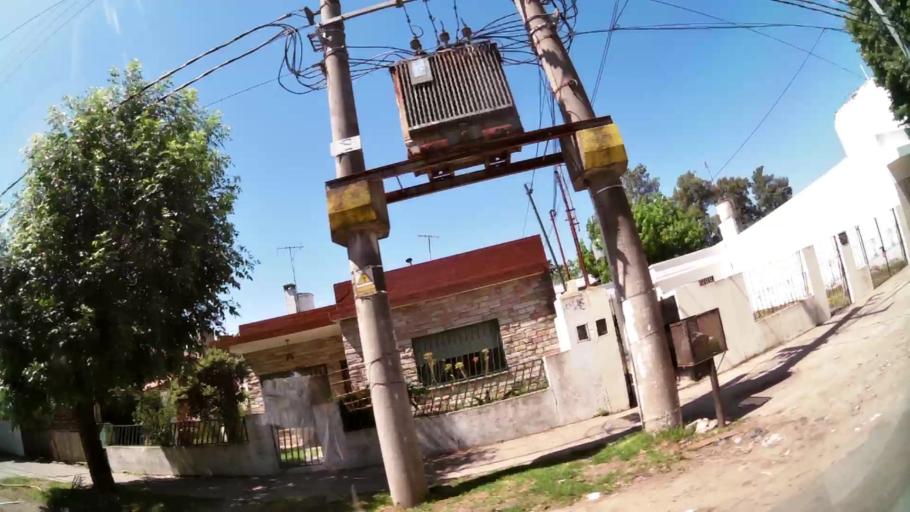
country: AR
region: Buenos Aires
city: Hurlingham
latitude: -34.5019
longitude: -58.6689
